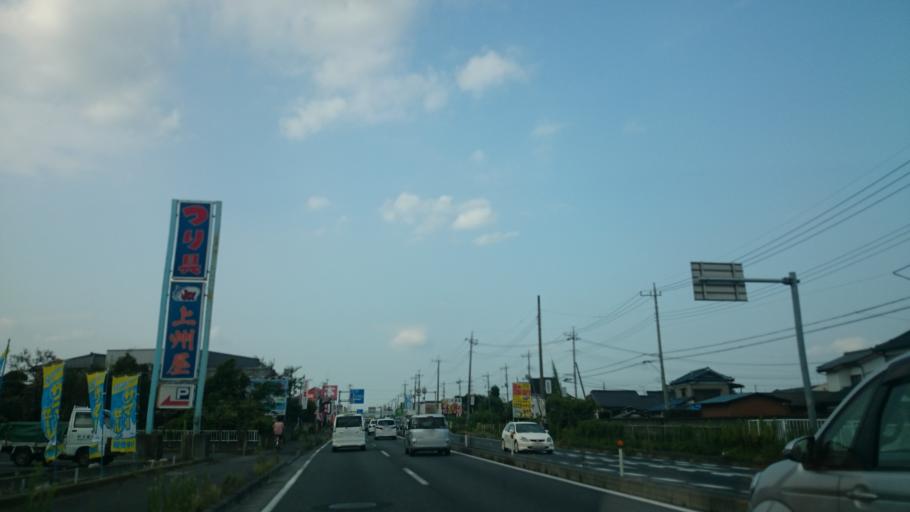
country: JP
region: Saitama
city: Kasukabe
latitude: 35.9633
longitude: 139.7319
